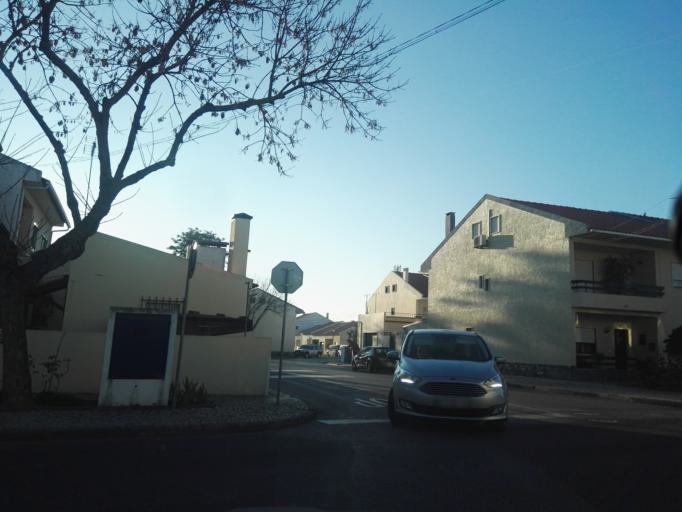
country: PT
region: Santarem
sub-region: Benavente
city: Samora Correia
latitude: 38.9320
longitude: -8.8671
